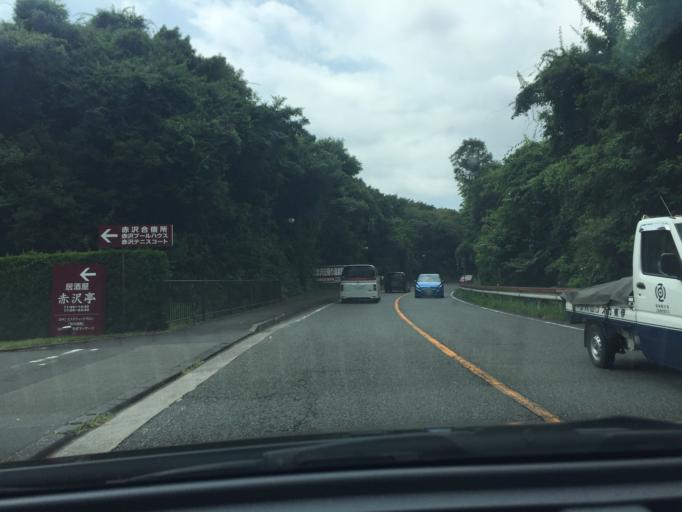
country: JP
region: Shizuoka
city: Ito
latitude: 34.8599
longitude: 139.0949
